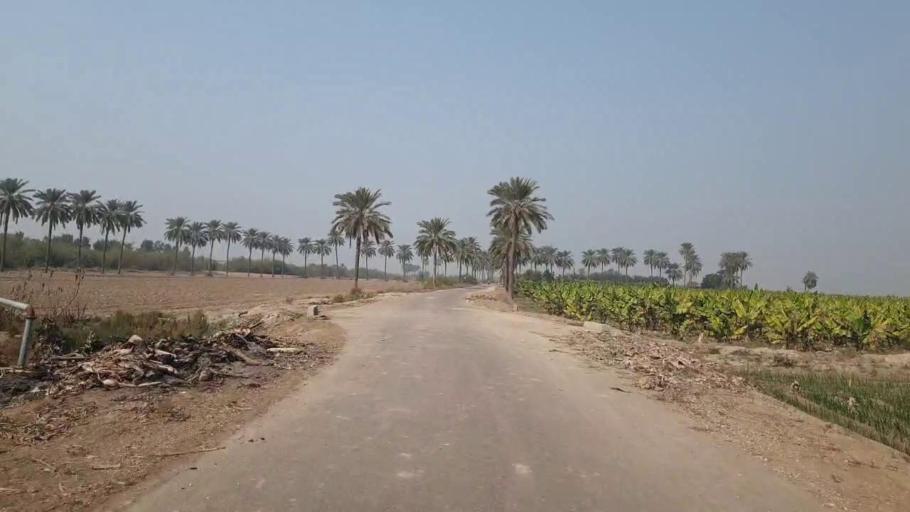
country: PK
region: Sindh
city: Bhit Shah
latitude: 25.7770
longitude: 68.4789
